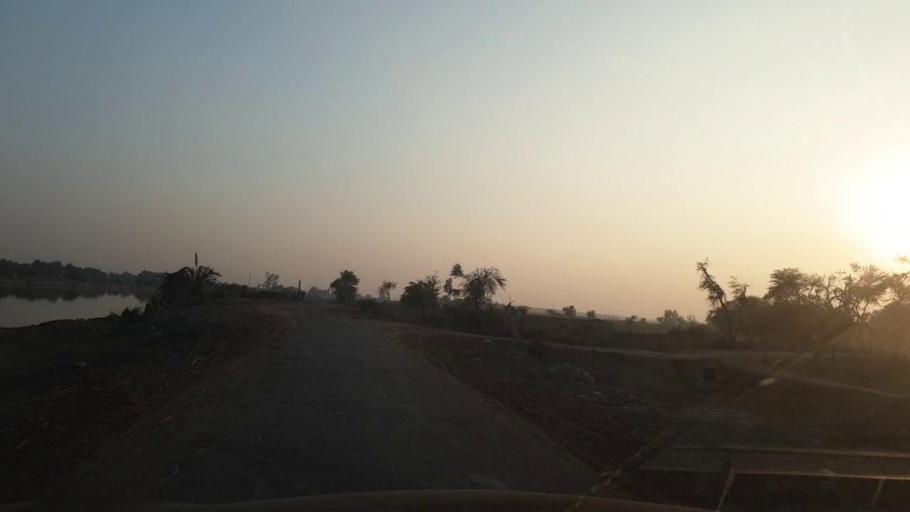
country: PK
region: Sindh
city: Ubauro
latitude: 28.2671
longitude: 69.7790
